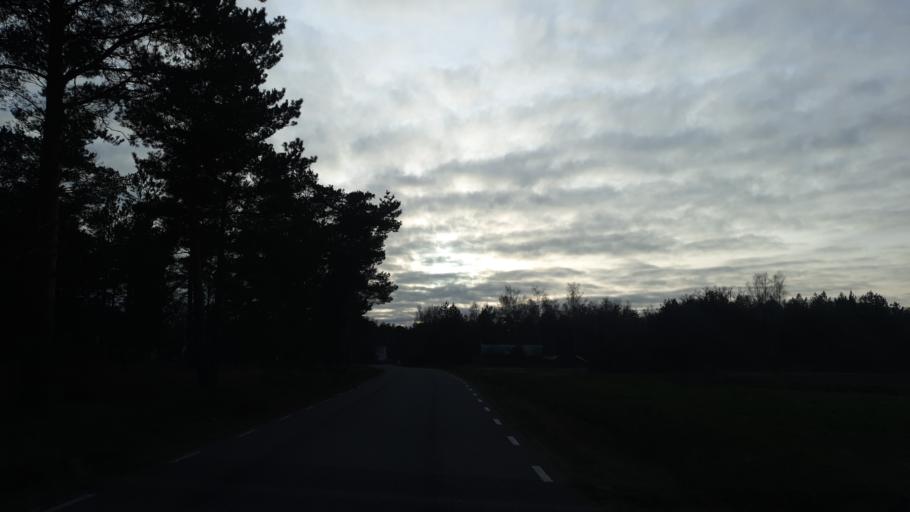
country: SE
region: Kalmar
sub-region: Torsas Kommun
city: Torsas
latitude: 56.3125
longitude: 16.0343
